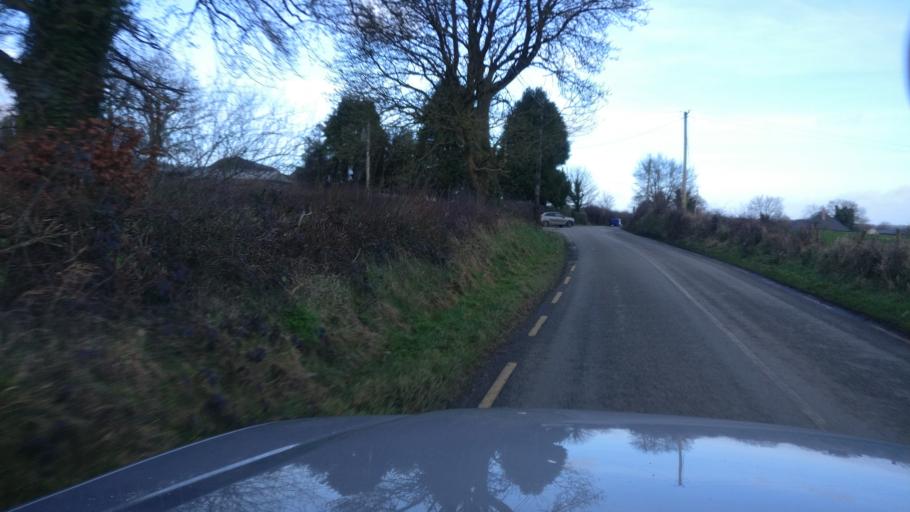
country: IE
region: Leinster
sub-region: Kilkenny
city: Castlecomer
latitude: 52.8310
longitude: -7.1997
